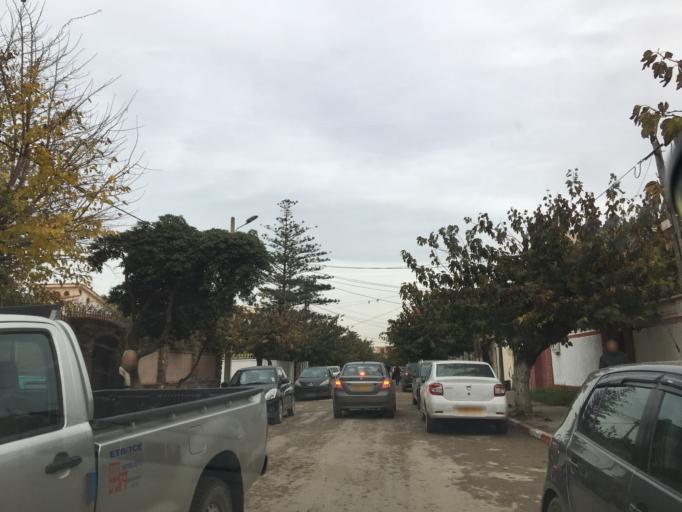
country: DZ
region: Alger
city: Ain Taya
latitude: 36.7922
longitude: 3.2376
